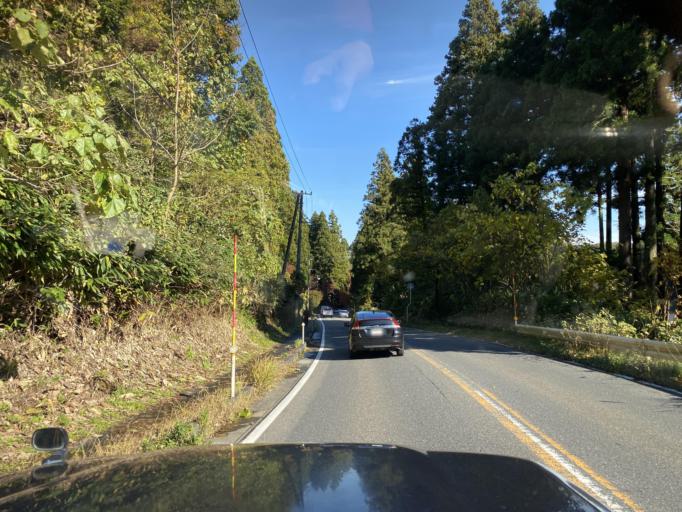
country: JP
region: Niigata
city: Niitsu-honcho
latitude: 37.7491
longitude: 139.1099
